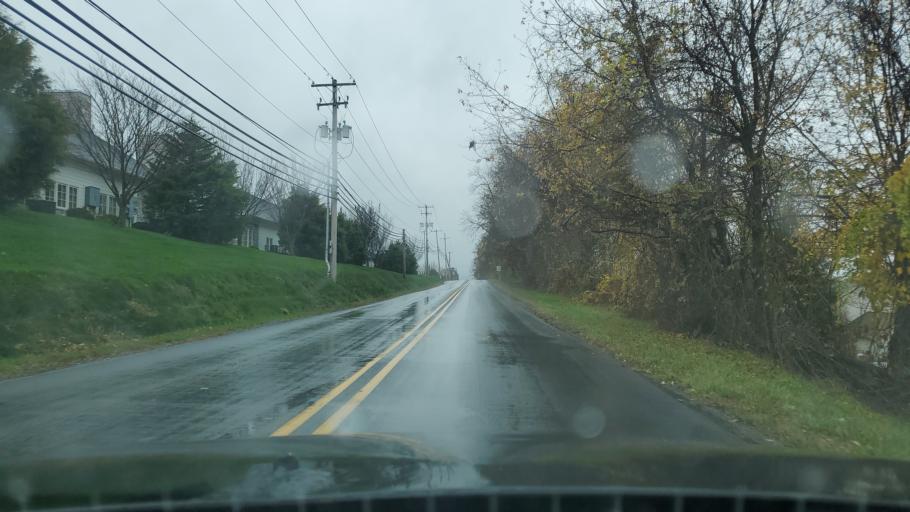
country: US
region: Pennsylvania
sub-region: Cumberland County
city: Mechanicsburg
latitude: 40.1702
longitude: -76.9964
